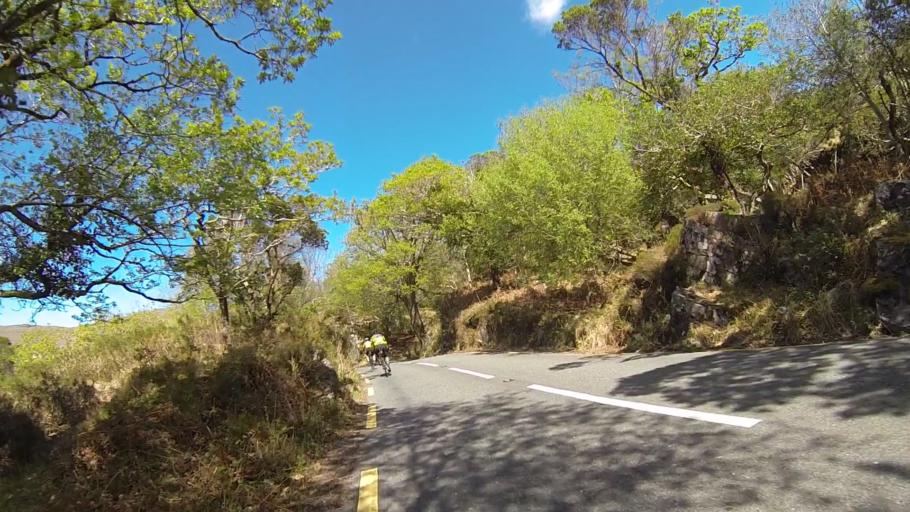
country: IE
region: Munster
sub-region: Ciarrai
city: Cill Airne
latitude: 51.9804
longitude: -9.5744
